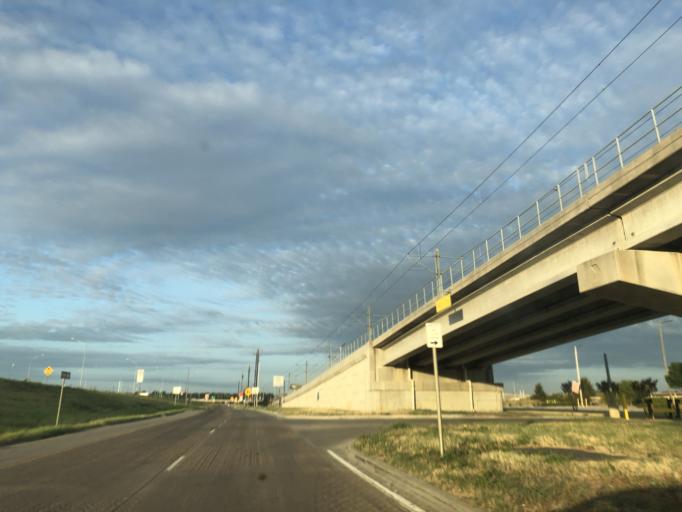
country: US
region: Texas
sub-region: Dallas County
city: Irving
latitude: 32.8456
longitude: -96.8973
